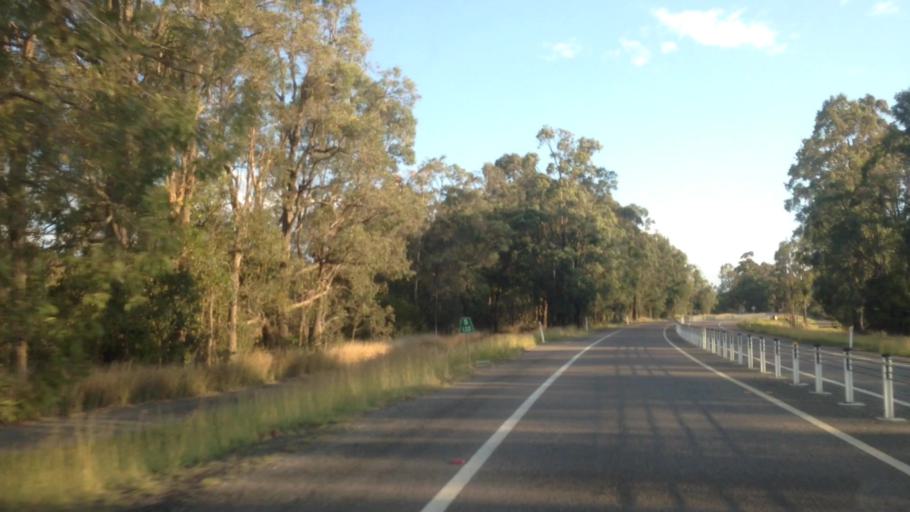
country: AU
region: New South Wales
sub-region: Lake Macquarie Shire
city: Cooranbong
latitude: -32.9556
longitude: 151.4809
